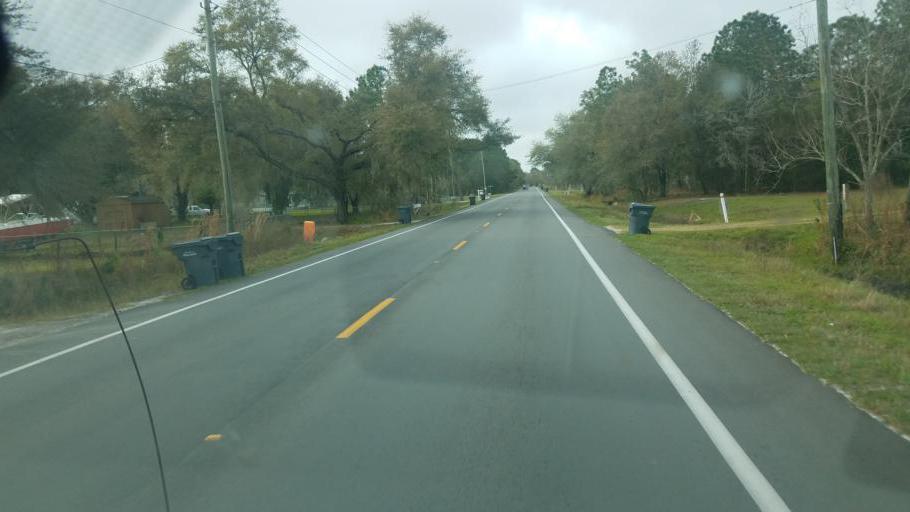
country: US
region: Florida
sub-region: Polk County
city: Kathleen
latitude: 28.2047
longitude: -81.9891
